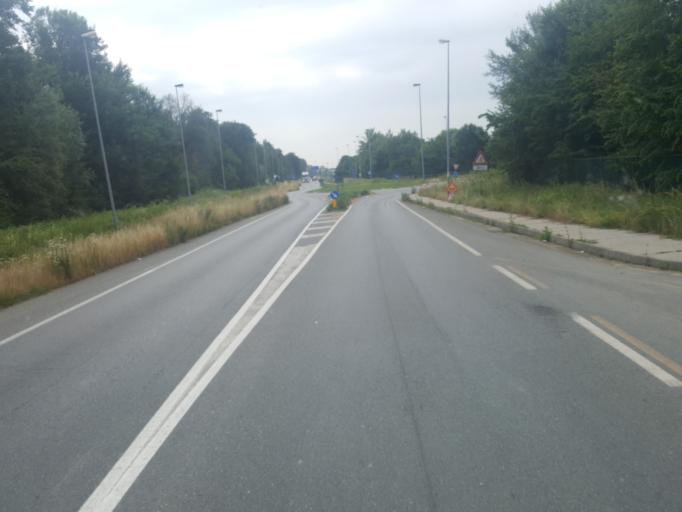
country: IT
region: Piedmont
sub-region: Provincia di Torino
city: Candiolo
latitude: 44.9689
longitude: 7.5663
